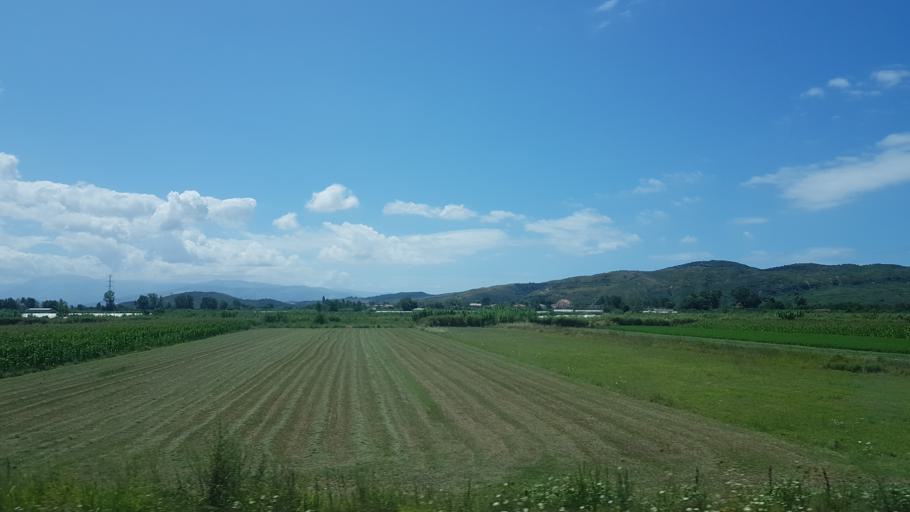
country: AL
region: Fier
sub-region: Rrethi i Fierit
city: Frakulla e Madhe
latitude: 40.6059
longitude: 19.5445
